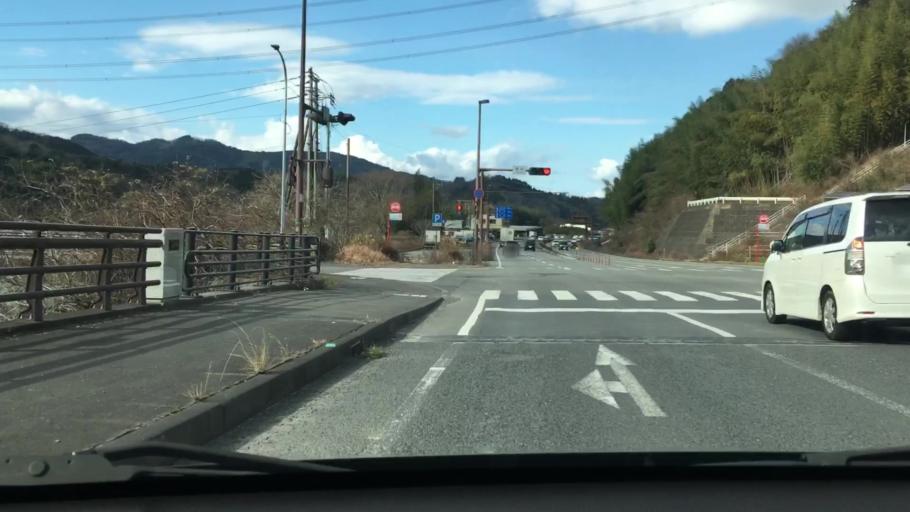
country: JP
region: Oita
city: Oita
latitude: 33.1128
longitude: 131.6560
